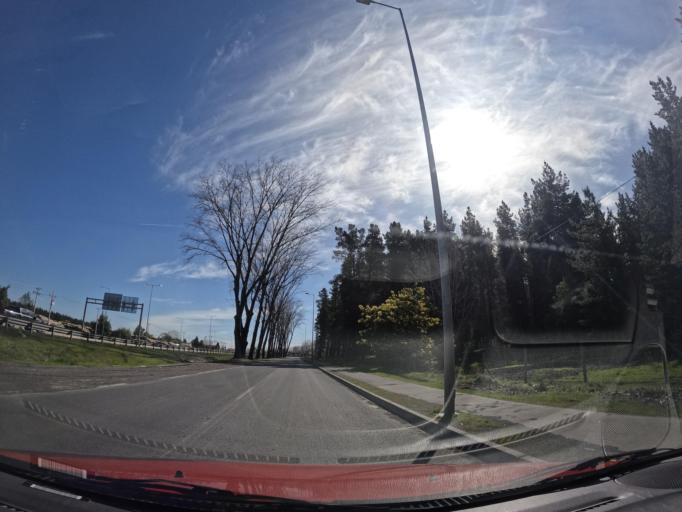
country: CL
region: Biobio
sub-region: Provincia de Biobio
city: Cabrero
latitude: -37.0331
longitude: -72.4185
